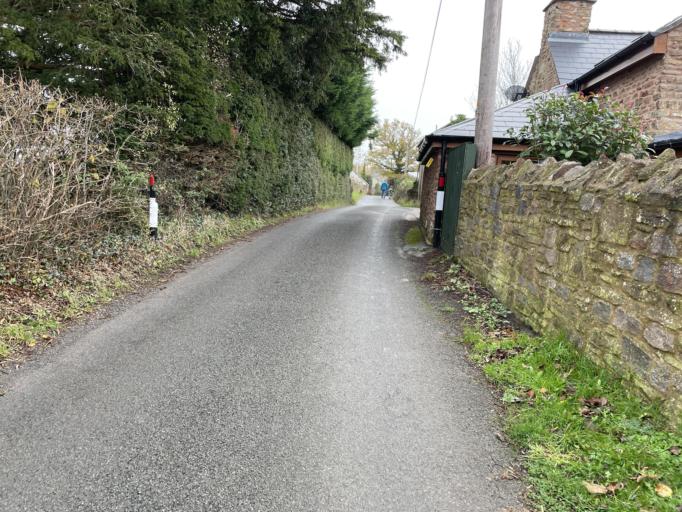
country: GB
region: England
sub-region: Herefordshire
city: Linton
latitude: 51.9209
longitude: -2.4893
